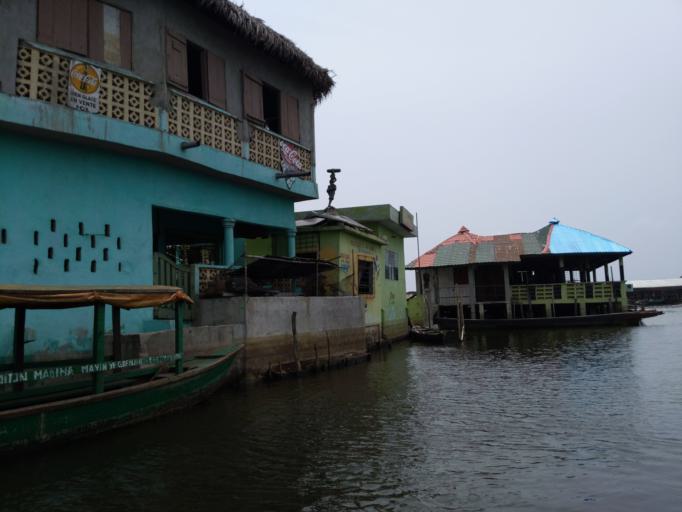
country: BJ
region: Atlantique
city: Abomey-Calavi
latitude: 6.4686
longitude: 2.3910
